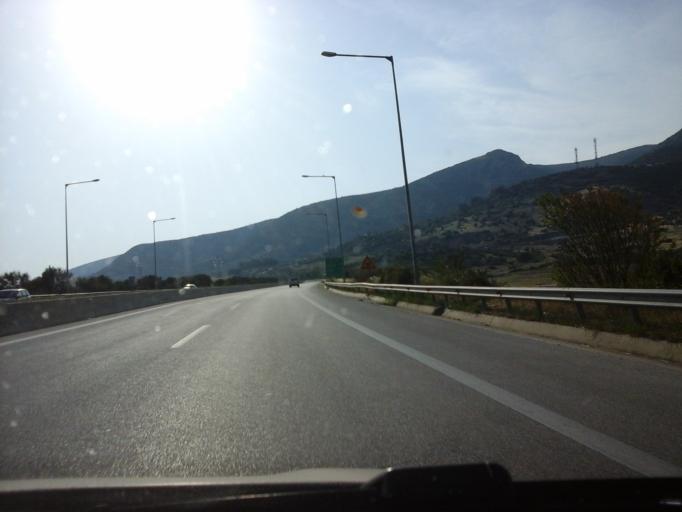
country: GR
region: East Macedonia and Thrace
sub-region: Nomos Kavalas
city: Chrysoupolis
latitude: 40.9895
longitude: 24.6271
